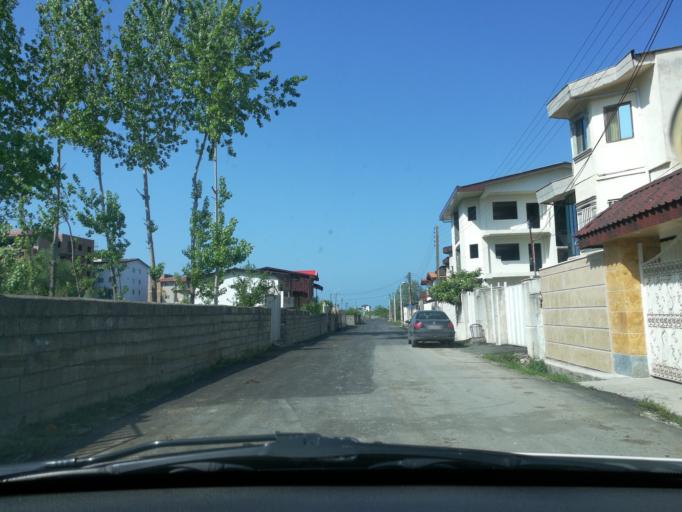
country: IR
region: Mazandaran
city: Chalus
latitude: 36.6696
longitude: 51.4321
